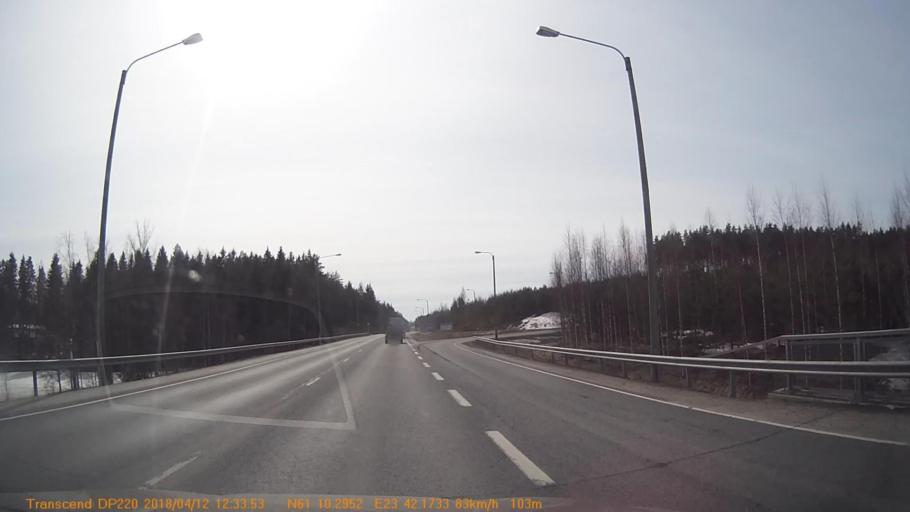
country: FI
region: Pirkanmaa
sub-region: Etelae-Pirkanmaa
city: Kylmaekoski
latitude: 61.1712
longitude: 23.7026
